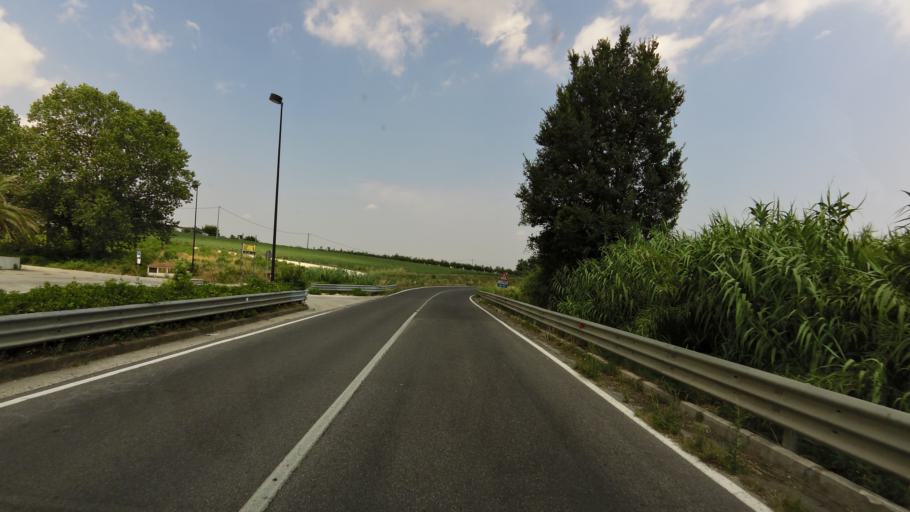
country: IT
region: The Marches
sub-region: Provincia di Ancona
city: Castelfidardo
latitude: 43.4812
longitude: 13.5786
